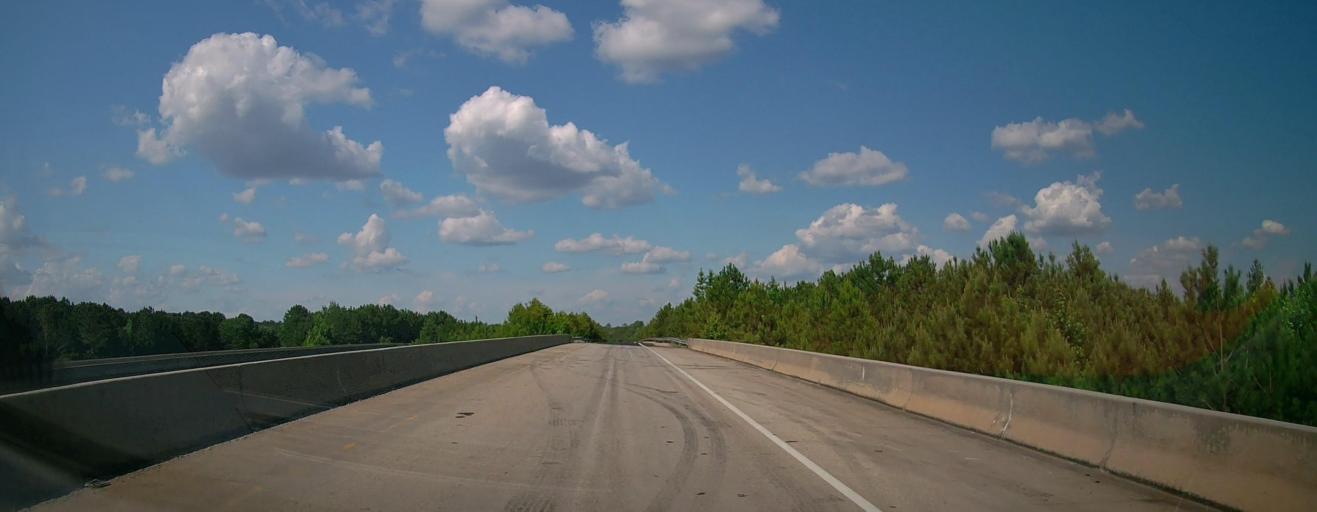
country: US
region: Georgia
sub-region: Henry County
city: Hampton
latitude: 33.3757
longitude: -84.2944
